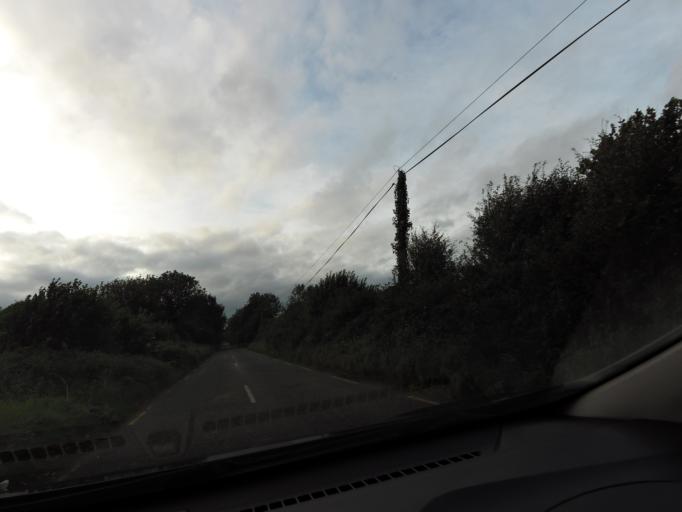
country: IE
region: Leinster
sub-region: Uibh Fhaili
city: Ferbane
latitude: 53.1815
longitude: -7.7348
